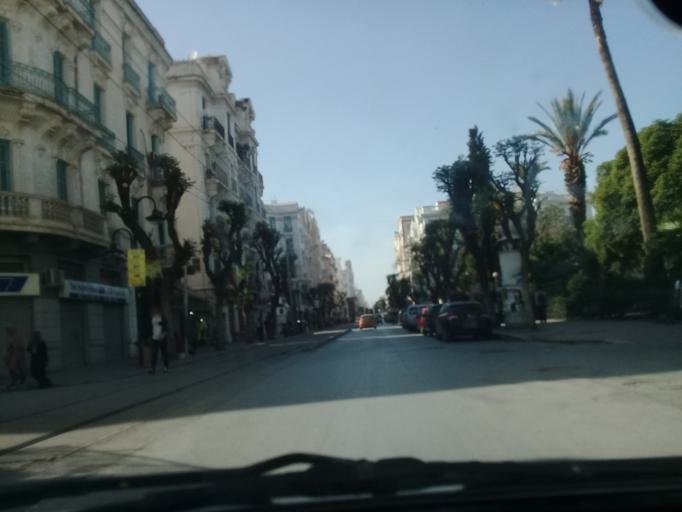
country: TN
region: Tunis
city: Tunis
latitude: 36.8035
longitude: 10.1808
